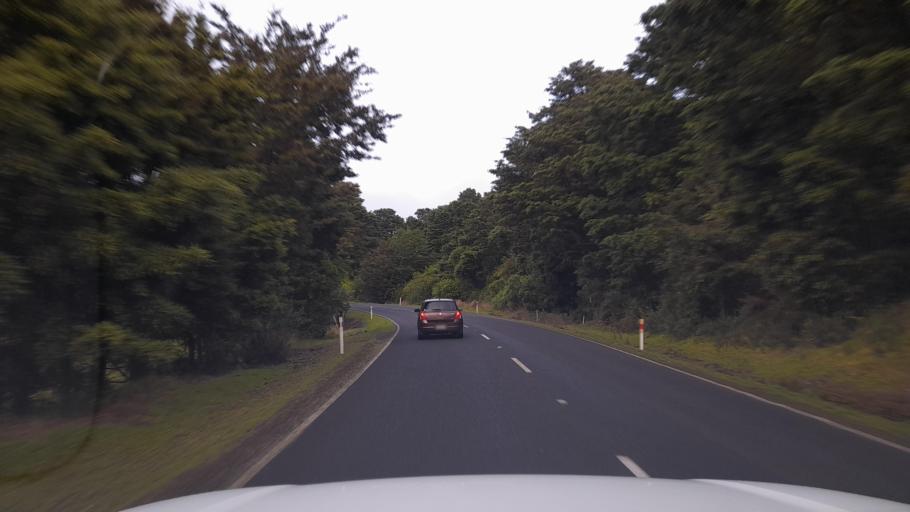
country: NZ
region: Northland
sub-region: Whangarei
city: Maungatapere
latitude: -35.7097
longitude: 173.9988
